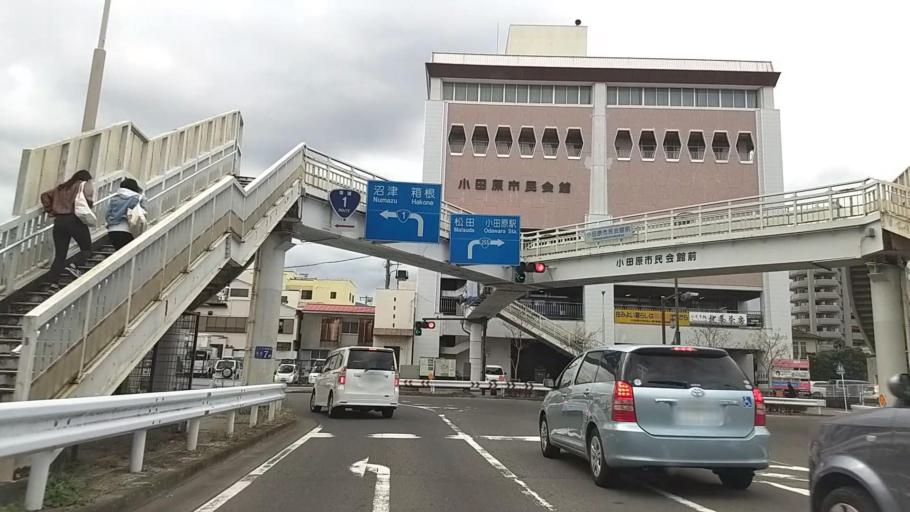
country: JP
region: Kanagawa
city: Odawara
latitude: 35.2506
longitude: 139.1594
